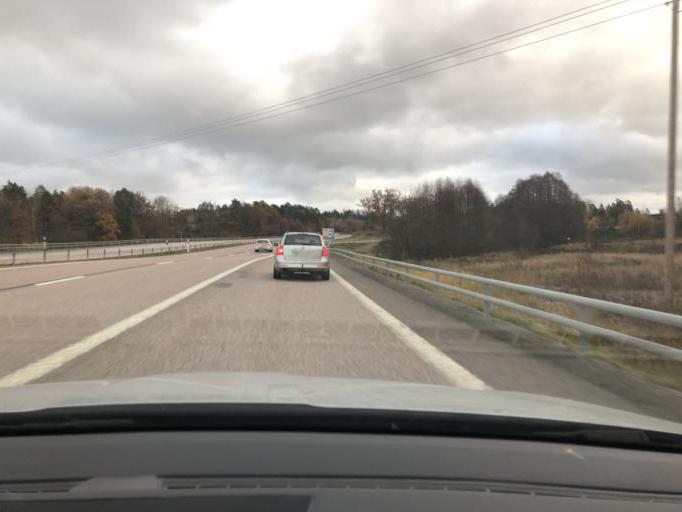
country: SE
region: Soedermanland
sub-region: Strangnas Kommun
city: Strangnas
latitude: 59.3685
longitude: 16.9450
